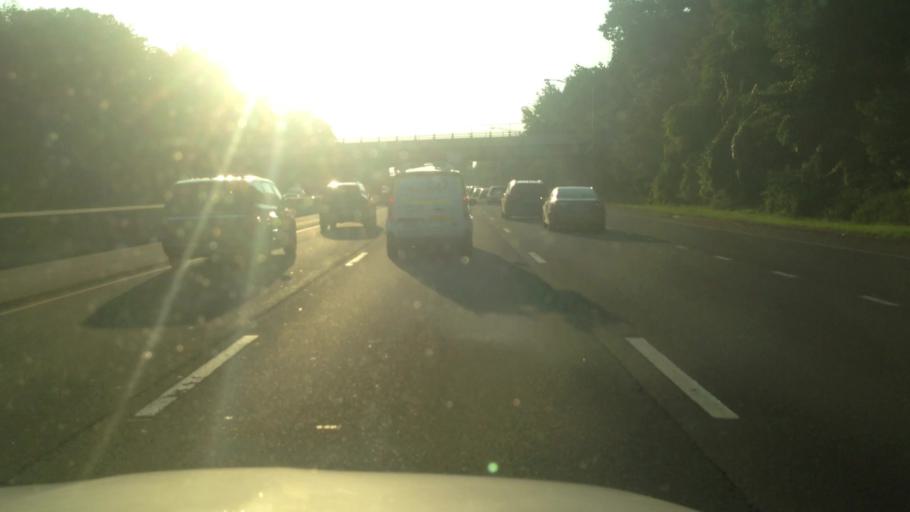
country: US
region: Connecticut
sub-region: New Haven County
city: Milford
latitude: 41.2355
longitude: -73.0445
